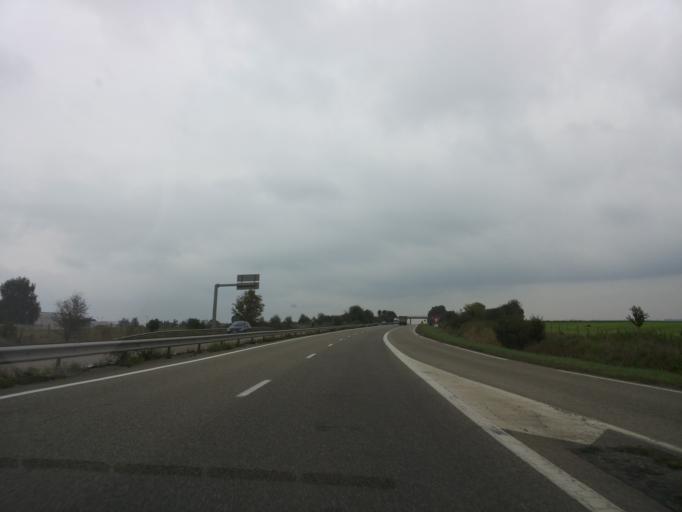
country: FR
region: Lorraine
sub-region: Departement de la Moselle
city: Phalsbourg
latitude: 48.7647
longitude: 7.2220
